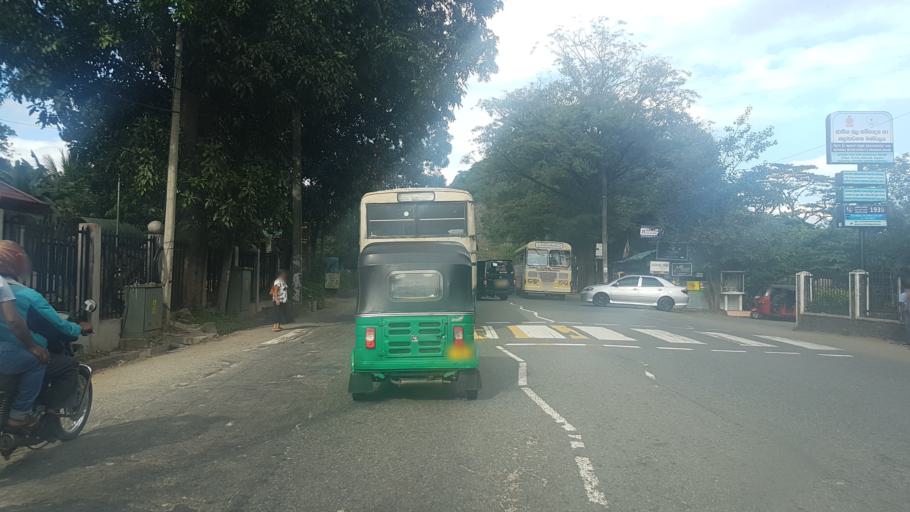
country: LK
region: Central
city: Kandy
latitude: 7.2699
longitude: 80.6049
